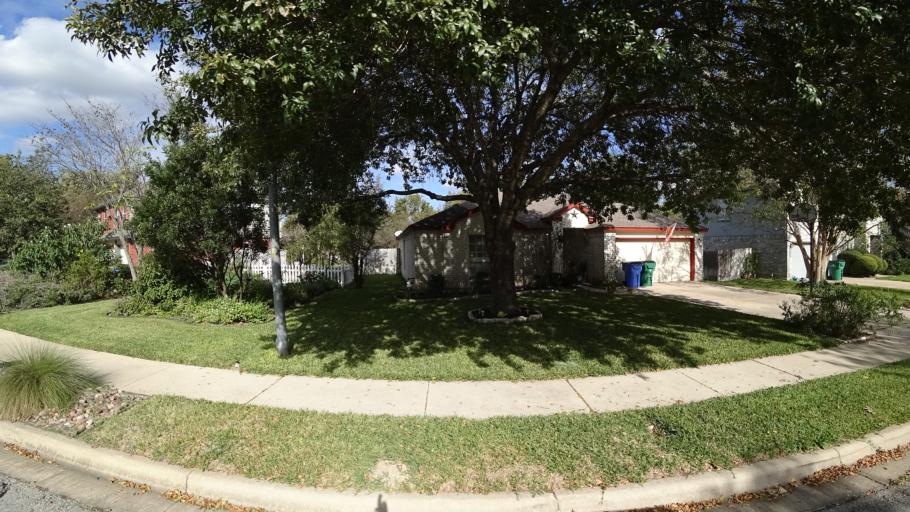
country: US
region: Texas
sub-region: Travis County
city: Pflugerville
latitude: 30.4358
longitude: -97.6360
